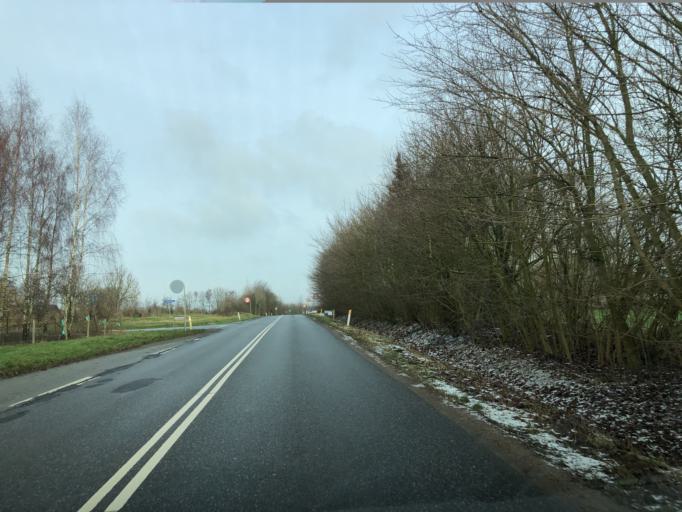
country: DK
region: South Denmark
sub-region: Vejle Kommune
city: Jelling
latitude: 55.7751
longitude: 9.4262
